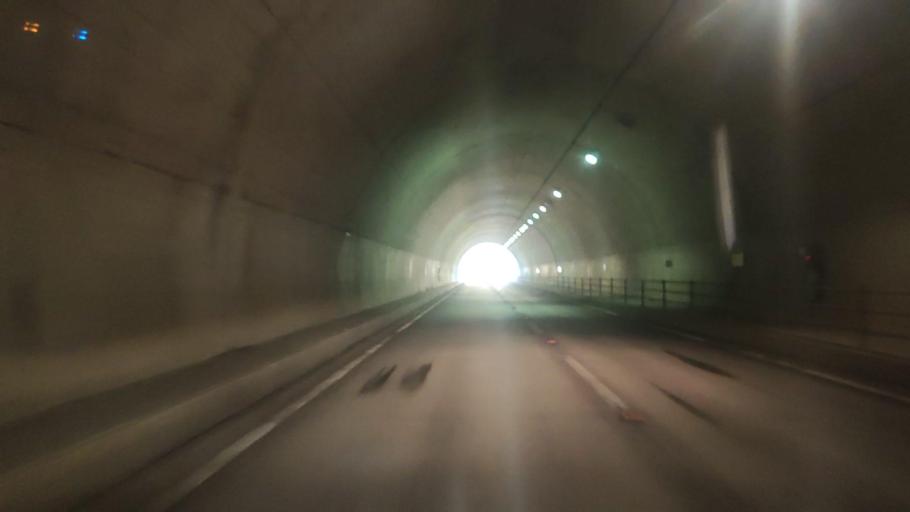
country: JP
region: Miyazaki
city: Nobeoka
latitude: 32.7385
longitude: 131.8246
